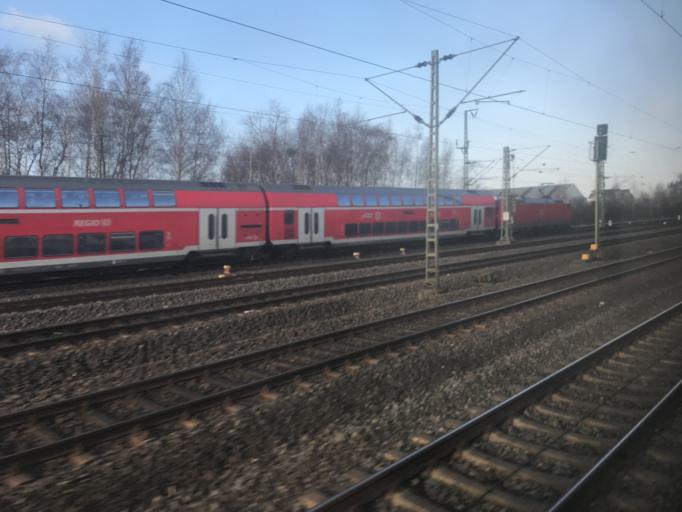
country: DE
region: North Rhine-Westphalia
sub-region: Regierungsbezirk Dusseldorf
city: Hochfeld
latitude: 51.3658
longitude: 6.7777
